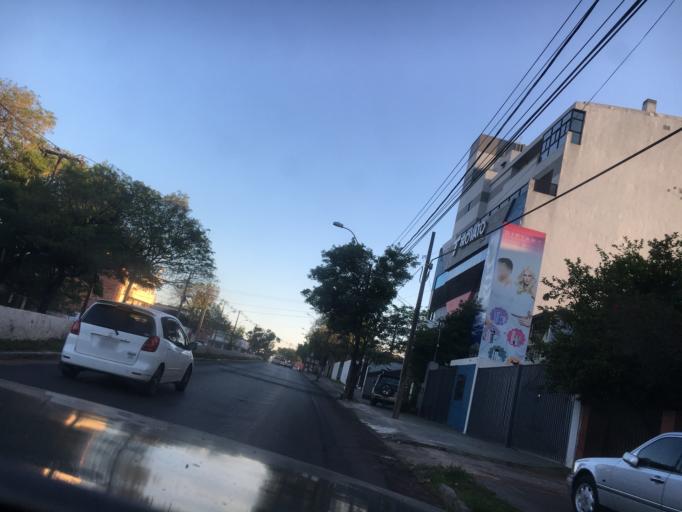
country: PY
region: Asuncion
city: Asuncion
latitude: -25.3035
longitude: -57.6320
